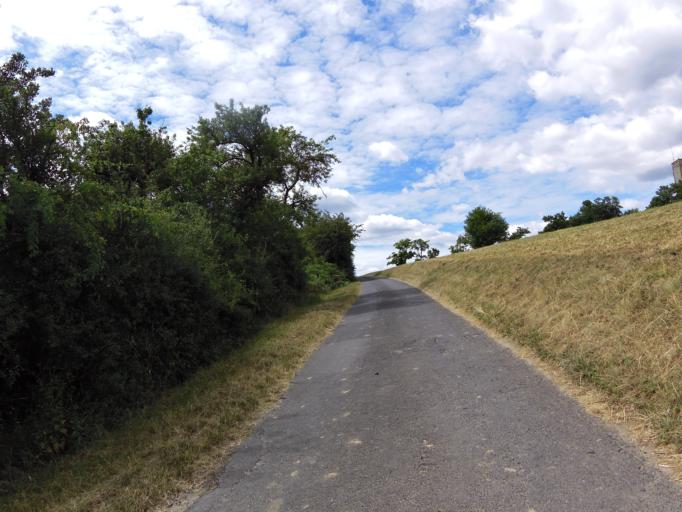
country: DE
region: Bavaria
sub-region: Regierungsbezirk Unterfranken
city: Veitshochheim
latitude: 49.8144
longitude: 9.8995
